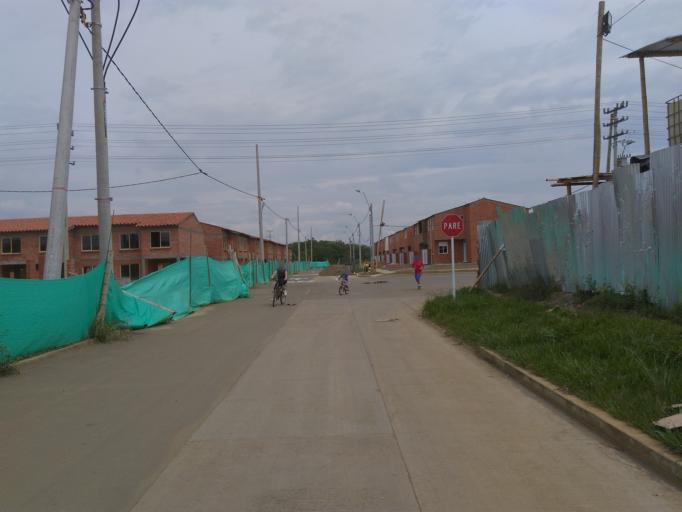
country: CO
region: Valle del Cauca
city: Jamundi
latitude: 3.2555
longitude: -76.5564
